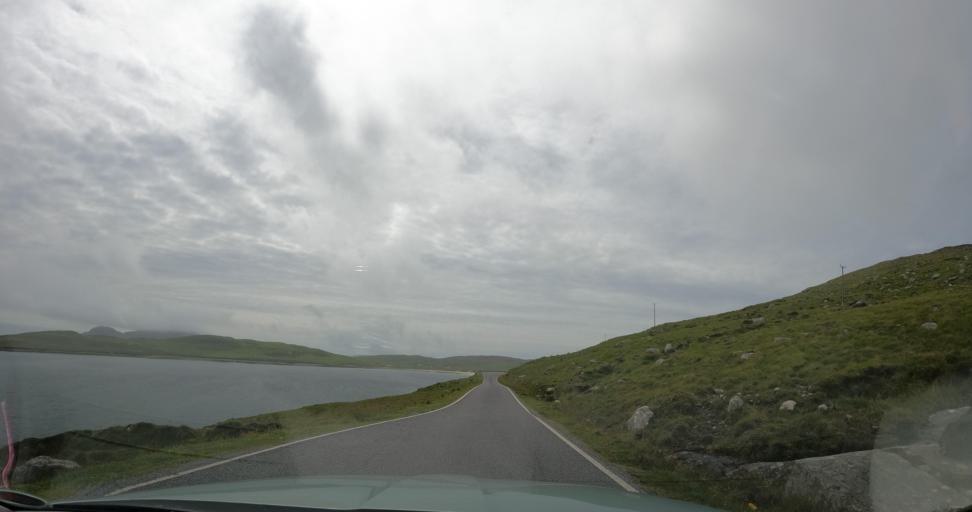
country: GB
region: Scotland
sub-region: Eilean Siar
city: Barra
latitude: 56.9309
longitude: -7.5242
